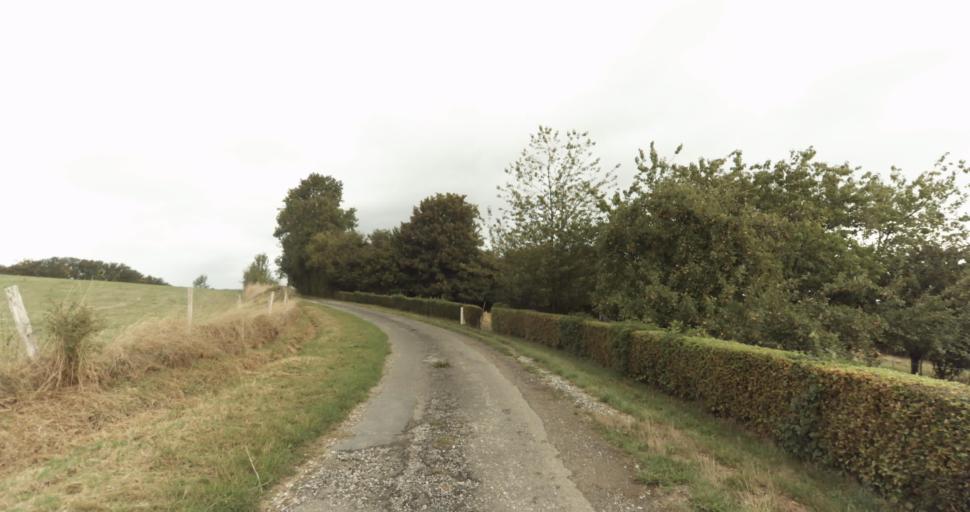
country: FR
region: Lower Normandy
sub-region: Departement de l'Orne
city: Sainte-Gauburge-Sainte-Colombe
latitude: 48.7188
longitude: 0.4526
